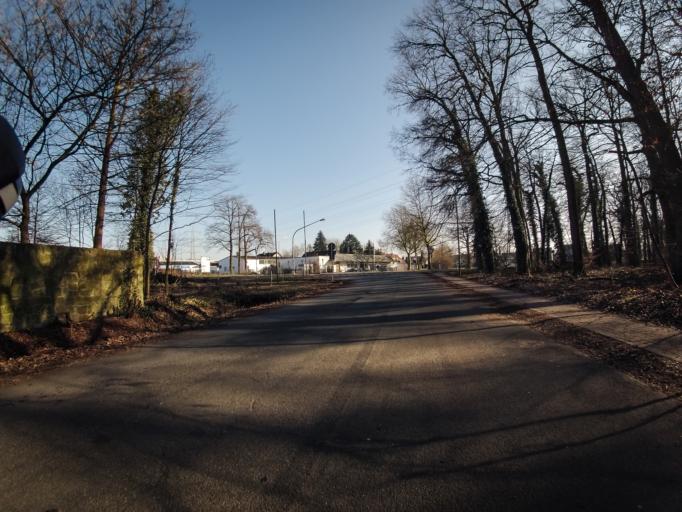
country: DE
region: Lower Saxony
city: Hasbergen
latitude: 52.2646
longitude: 7.9576
